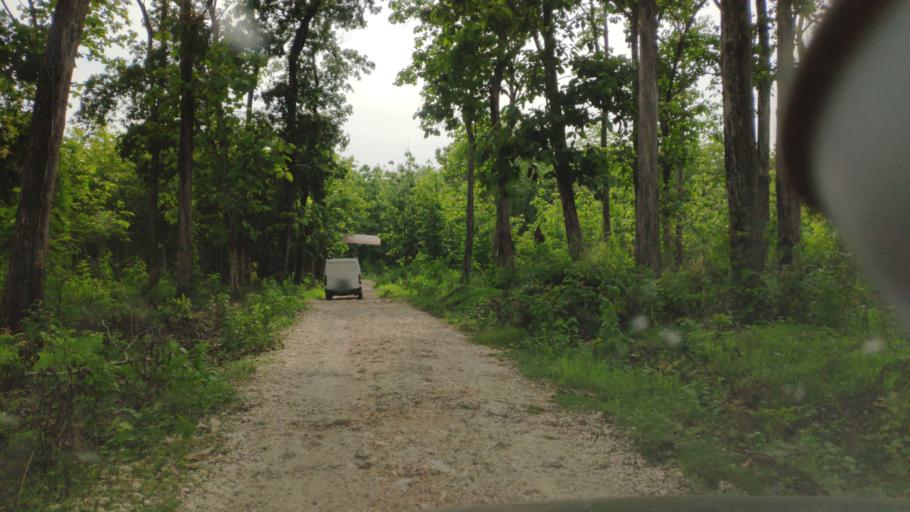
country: ID
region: Central Java
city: Randublatung
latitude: -7.2882
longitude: 111.2987
